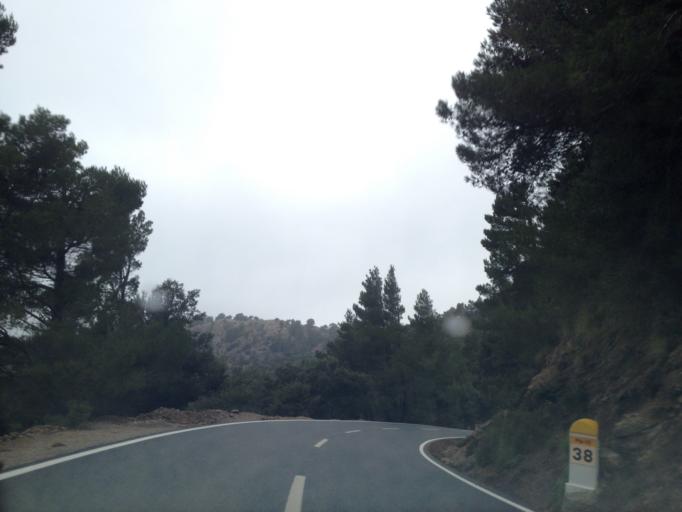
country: ES
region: Balearic Islands
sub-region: Illes Balears
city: Fornalutx
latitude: 39.7965
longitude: 2.7760
